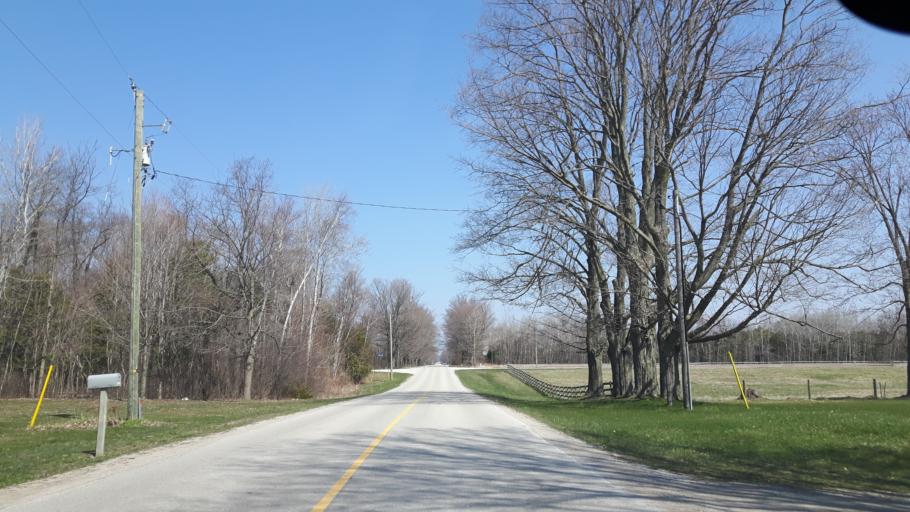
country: CA
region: Ontario
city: Goderich
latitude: 43.6229
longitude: -81.6846
